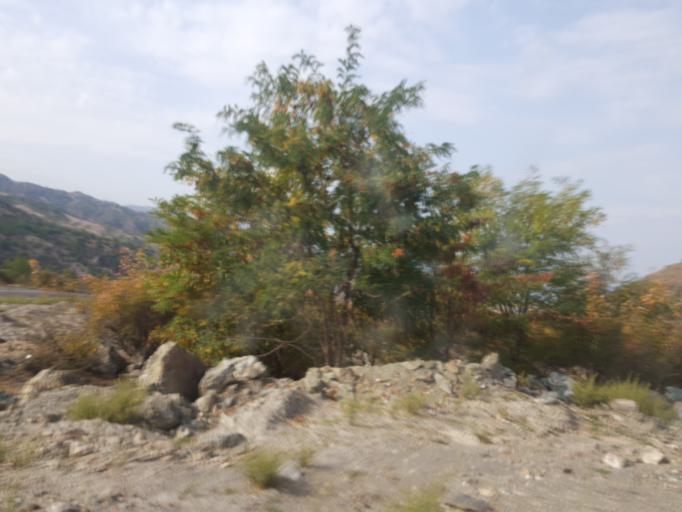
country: TR
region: Corum
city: Kamil
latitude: 41.1064
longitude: 34.7423
